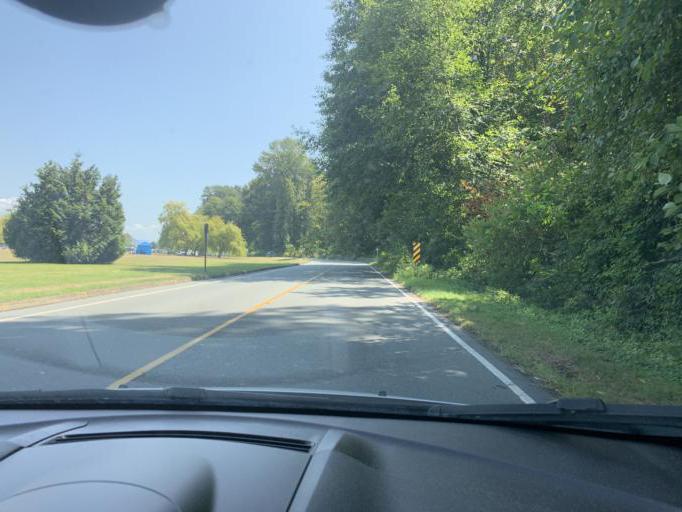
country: CA
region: British Columbia
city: West End
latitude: 49.2785
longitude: -123.2355
